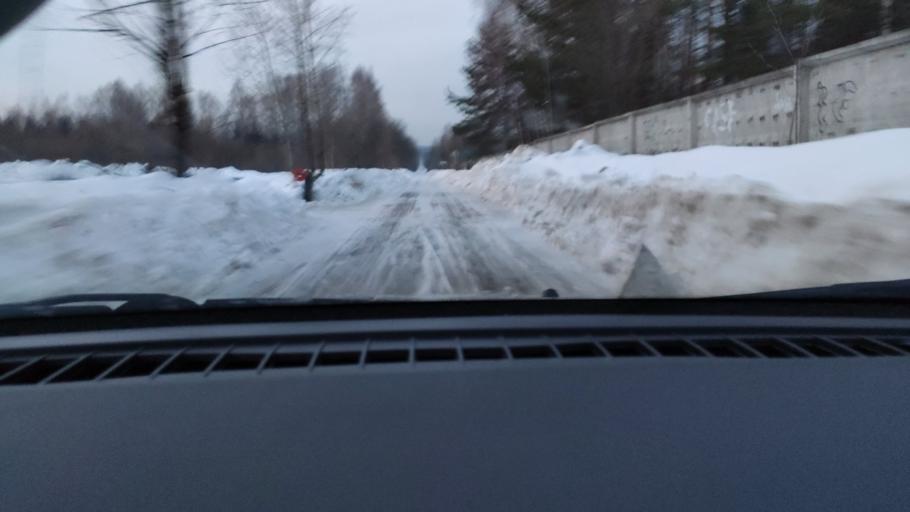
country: RU
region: Perm
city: Kondratovo
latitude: 58.0652
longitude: 56.1260
